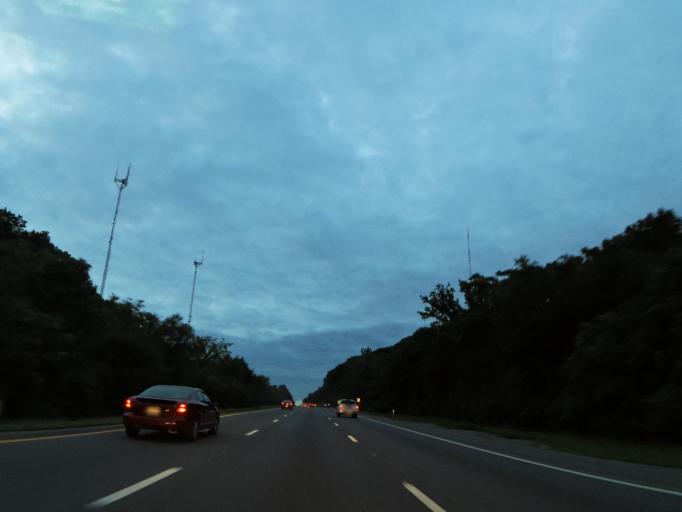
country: US
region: Tennessee
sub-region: Davidson County
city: Nashville
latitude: 36.2584
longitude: -86.7875
